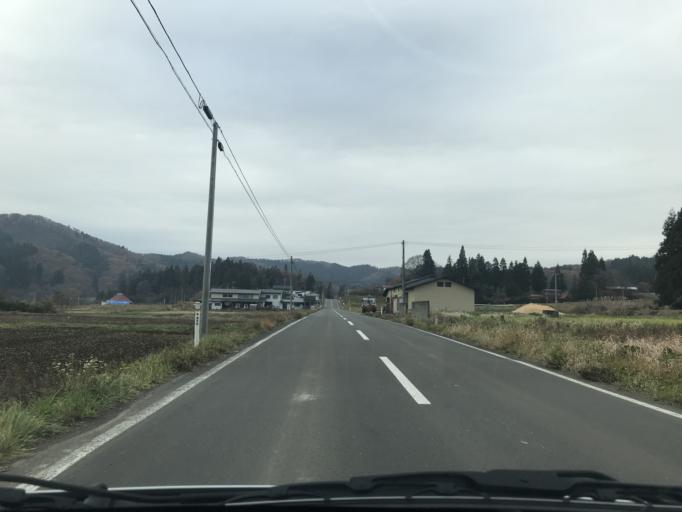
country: JP
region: Iwate
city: Kitakami
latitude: 39.2604
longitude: 141.1966
